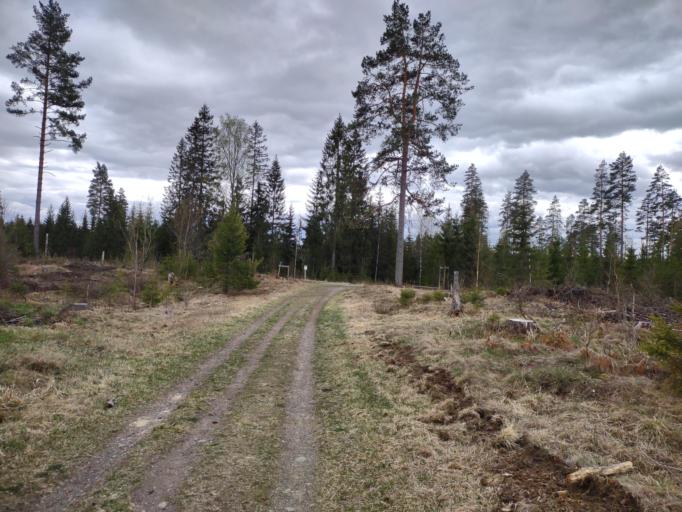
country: NO
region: Akershus
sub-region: Eidsvoll
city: Raholt
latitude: 60.2609
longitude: 11.1412
